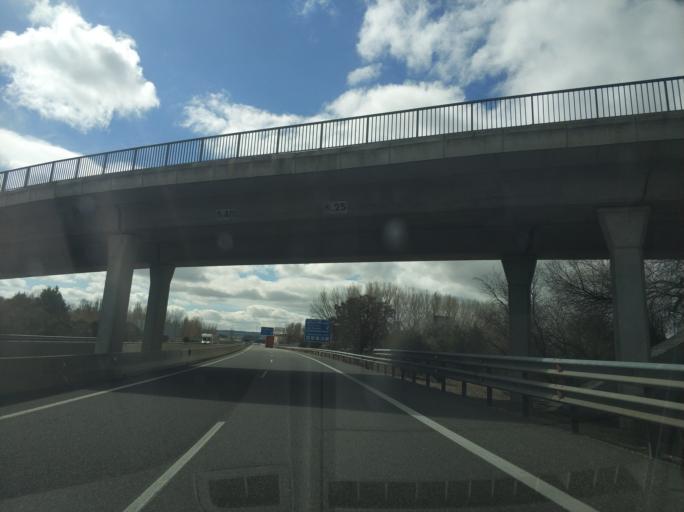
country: ES
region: Castille and Leon
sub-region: Provincia de Palencia
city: Quintana del Puente
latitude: 42.0895
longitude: -4.2099
